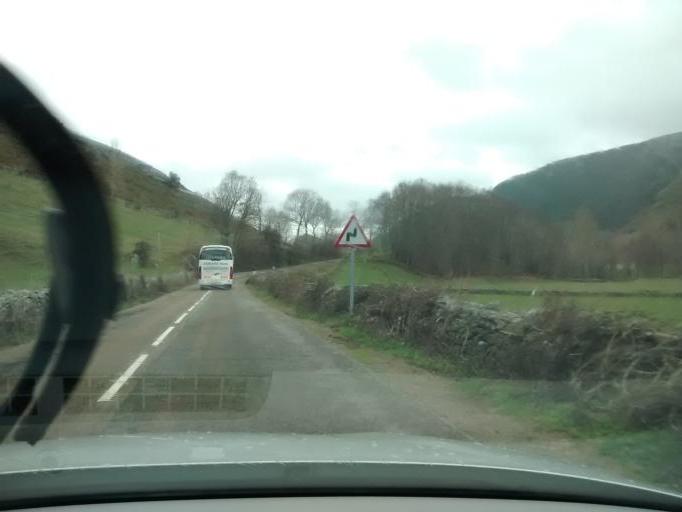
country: ES
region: Castille and Leon
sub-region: Provincia de Burgos
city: Espinosa de los Monteros
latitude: 43.1047
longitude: -3.5726
